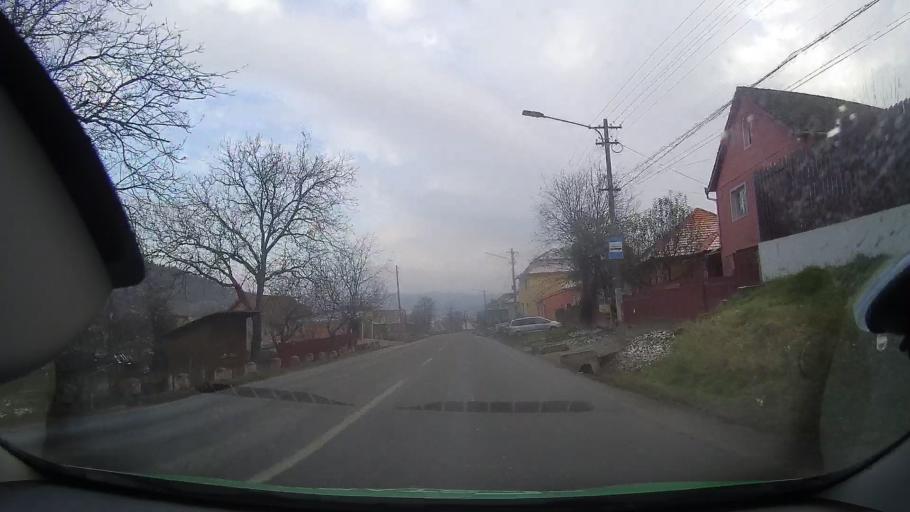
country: RO
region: Mures
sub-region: Municipiul Tarnaveni
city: Tarnaveni
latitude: 46.3385
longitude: 24.2840
